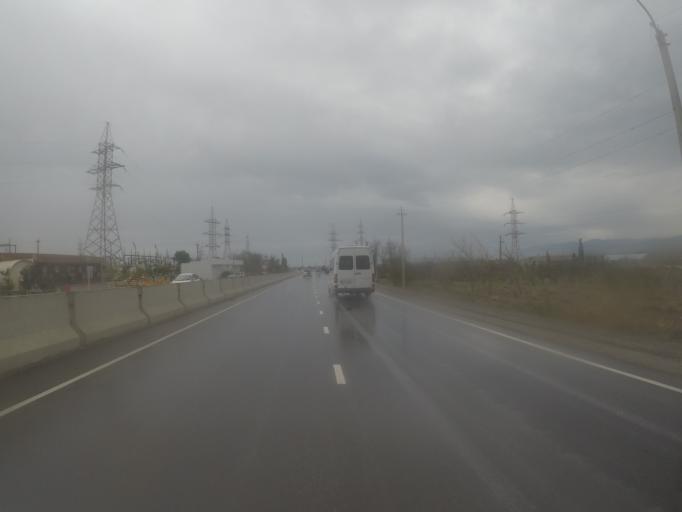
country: KG
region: Ysyk-Koel
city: Balykchy
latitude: 42.4549
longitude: 76.1540
